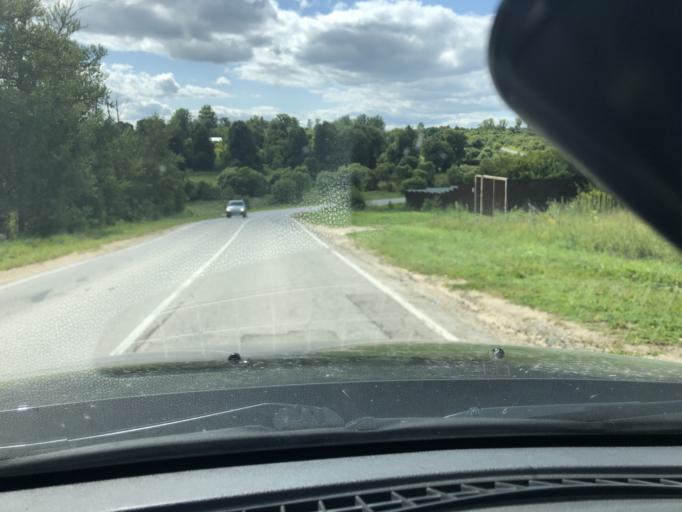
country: RU
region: Tula
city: Revyakino
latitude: 54.3461
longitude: 37.6152
